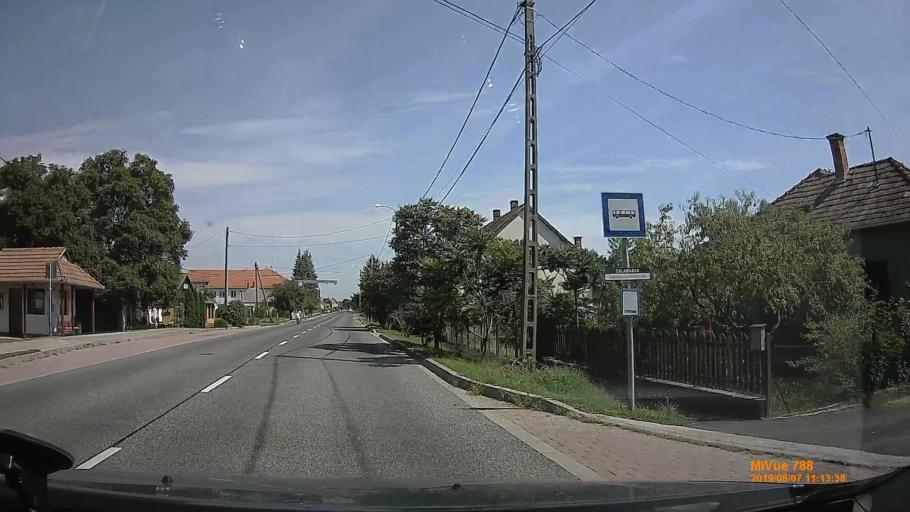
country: HU
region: Zala
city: Lenti
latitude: 46.7011
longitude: 16.5488
